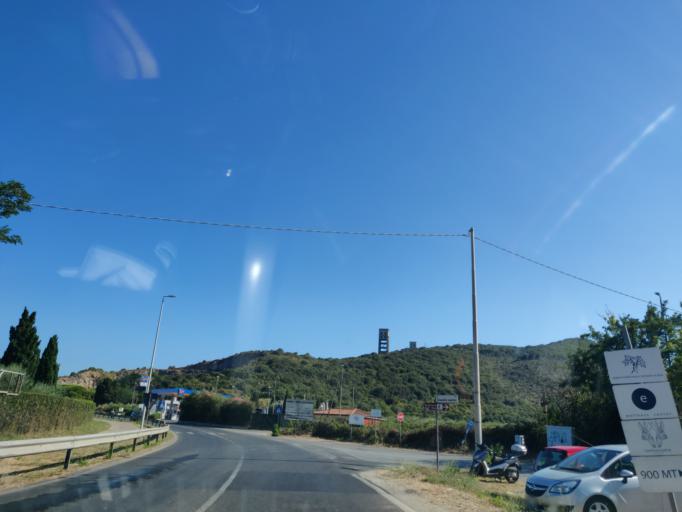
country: IT
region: Tuscany
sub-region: Provincia di Grosseto
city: Porto Ercole
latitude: 42.4267
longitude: 11.1969
